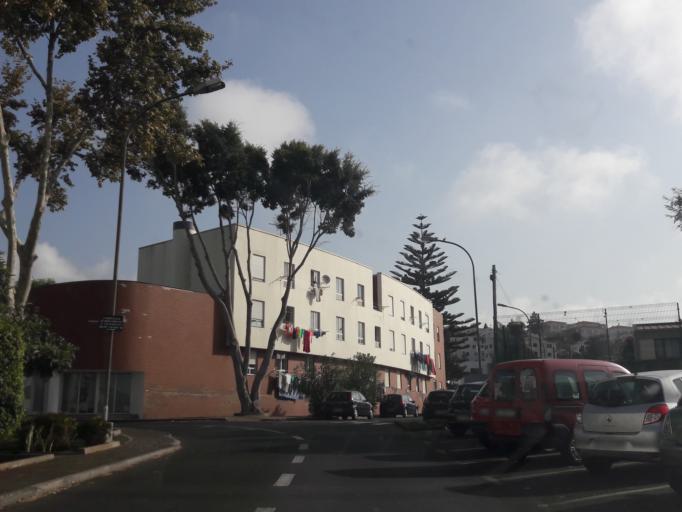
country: PT
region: Madeira
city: Camara de Lobos
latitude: 32.6580
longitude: -16.9462
